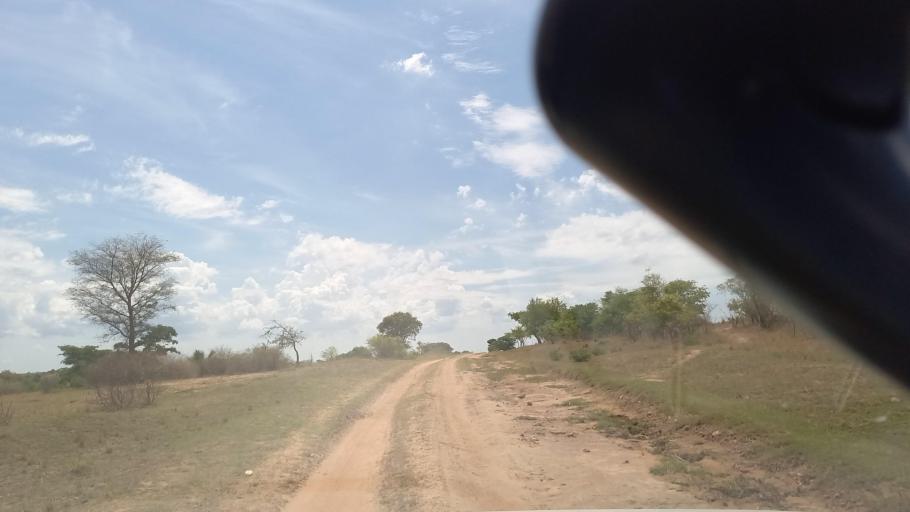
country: ZM
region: Southern
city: Mazabuka
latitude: -16.1397
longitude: 27.7616
